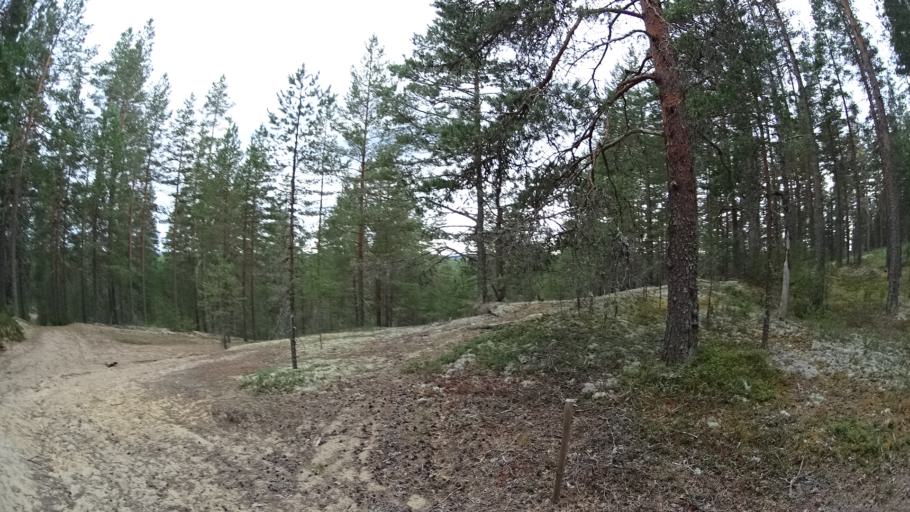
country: FI
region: Satakunta
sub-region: Pohjois-Satakunta
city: Jaemijaervi
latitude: 61.7704
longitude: 22.7431
